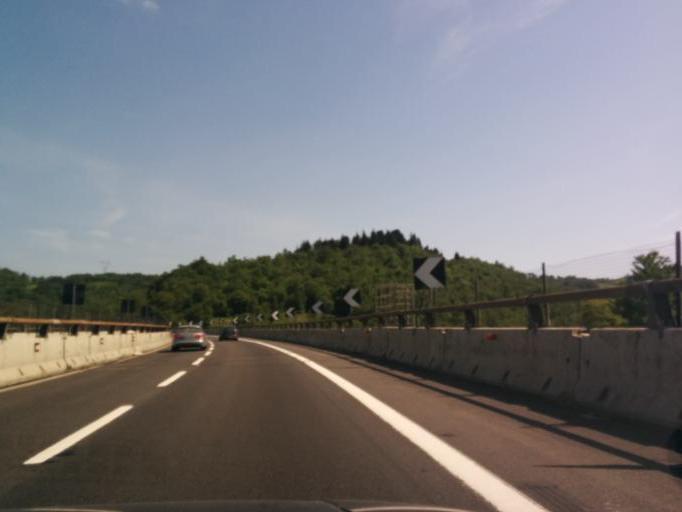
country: IT
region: Tuscany
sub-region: Province of Florence
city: Cavallina
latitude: 43.9352
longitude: 11.2218
